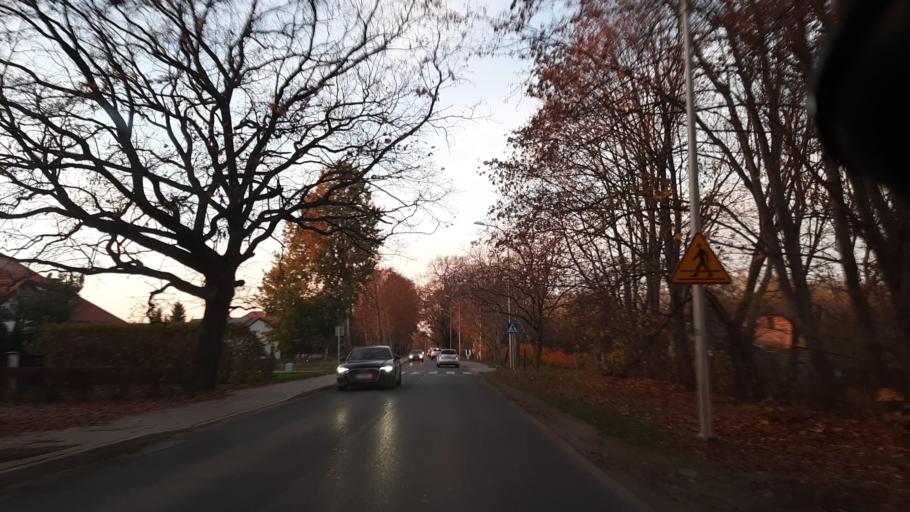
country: PL
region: Lublin Voivodeship
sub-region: Powiat lubelski
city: Lublin
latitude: 51.2786
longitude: 22.5053
